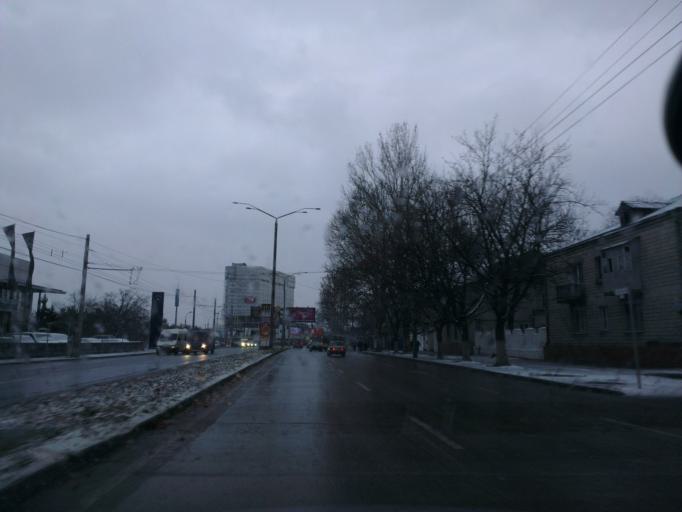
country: MD
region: Chisinau
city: Chisinau
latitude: 47.0475
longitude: 28.8491
